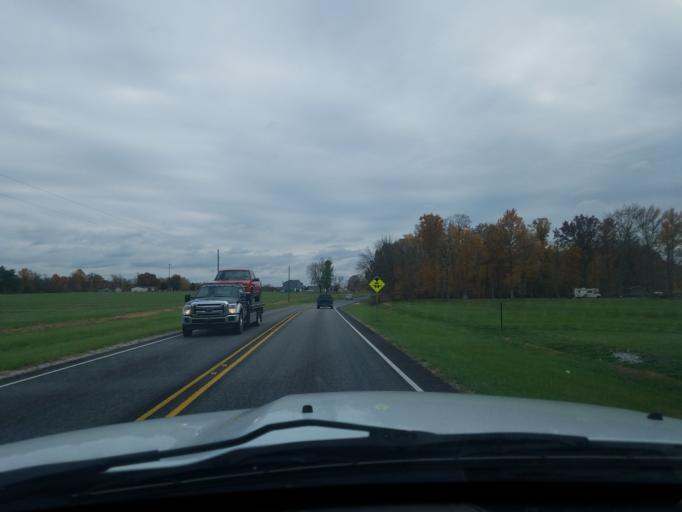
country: US
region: Indiana
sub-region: Jackson County
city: Seymour
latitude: 38.8977
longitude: -85.8190
